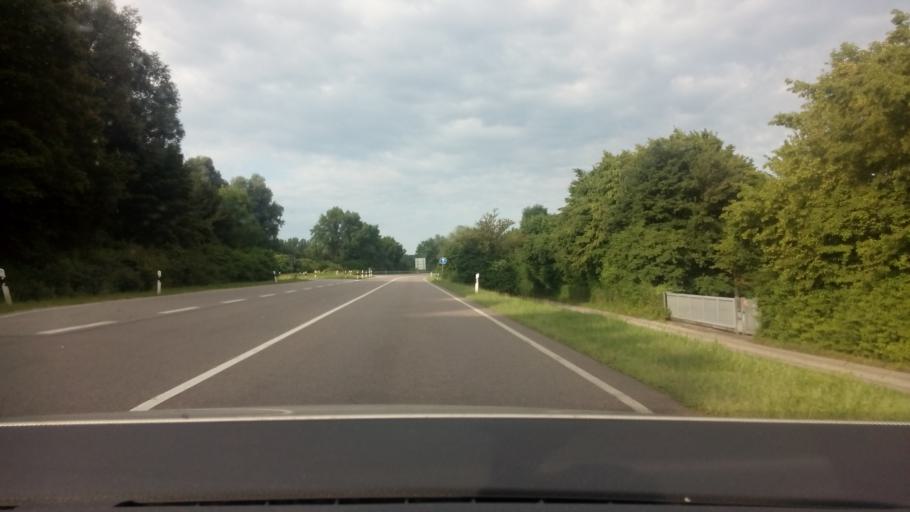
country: DE
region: Bavaria
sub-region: Upper Bavaria
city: Karlsfeld
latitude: 48.2461
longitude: 11.4757
